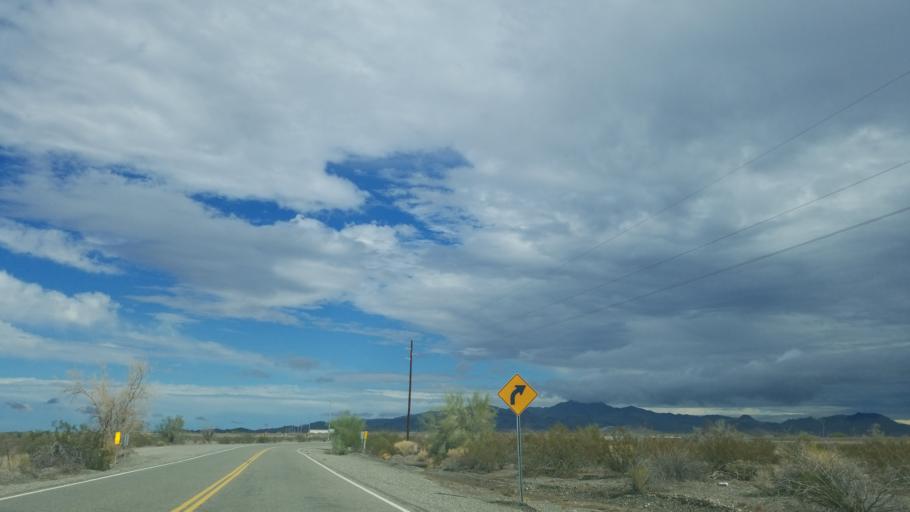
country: US
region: Arizona
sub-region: La Paz County
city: Salome
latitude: 33.7284
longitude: -113.7663
